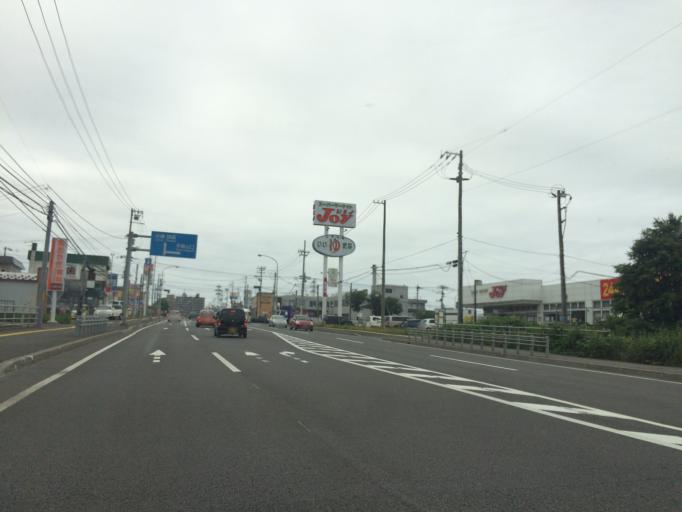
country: JP
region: Hokkaido
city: Sapporo
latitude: 43.1272
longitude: 141.2158
